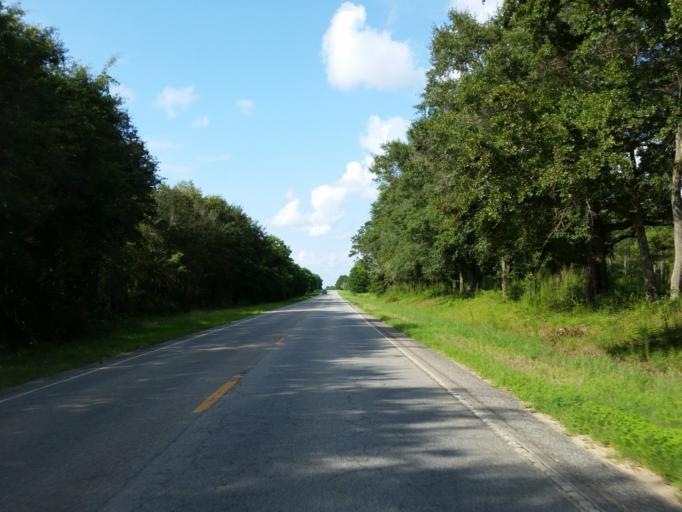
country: US
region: Georgia
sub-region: Lee County
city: Leesburg
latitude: 31.7970
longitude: -84.1247
